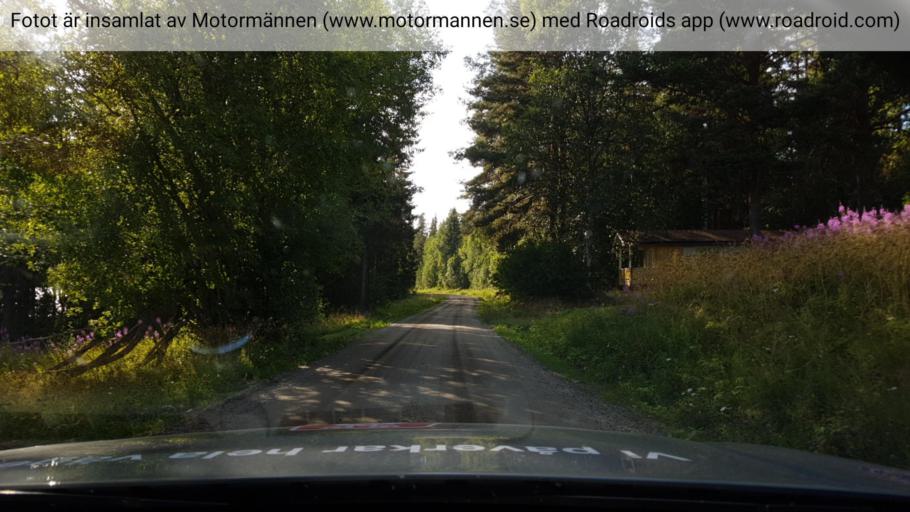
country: SE
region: Jaemtland
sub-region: Stroemsunds Kommun
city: Stroemsund
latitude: 63.7285
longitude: 16.0019
